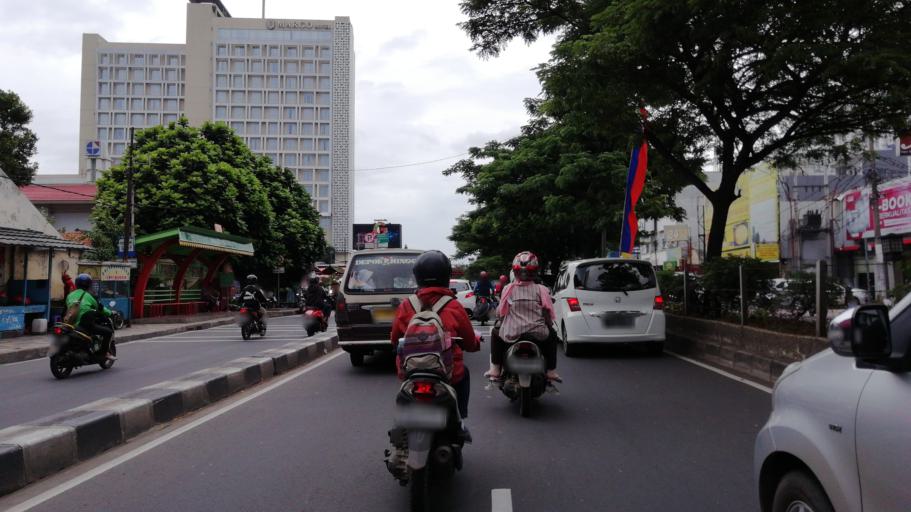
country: ID
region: West Java
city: Depok
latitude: -6.3703
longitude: 106.8336
